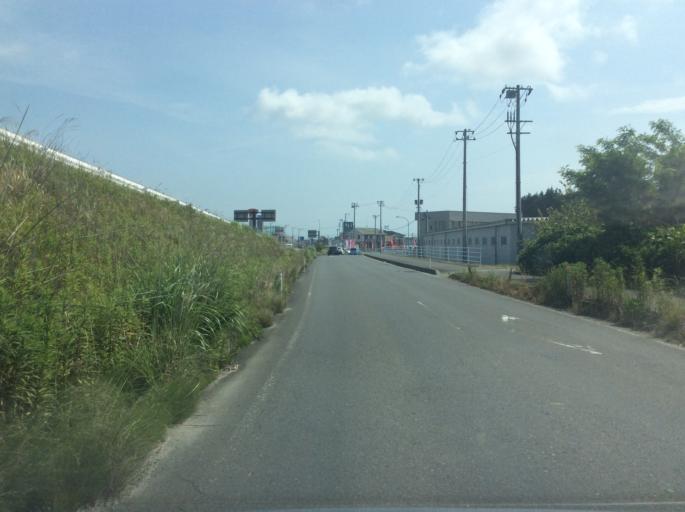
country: JP
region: Fukushima
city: Iwaki
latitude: 37.0630
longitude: 140.9407
